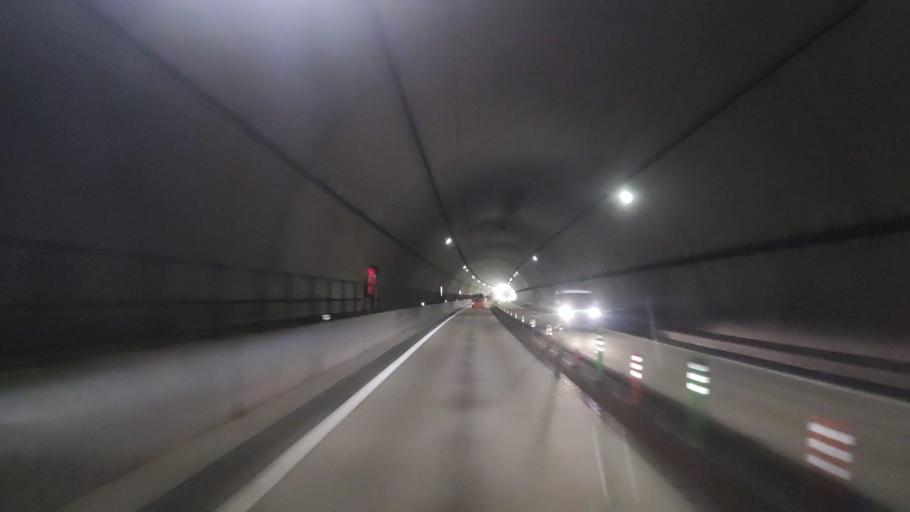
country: JP
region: Wakayama
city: Tanabe
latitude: 33.5945
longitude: 135.4361
